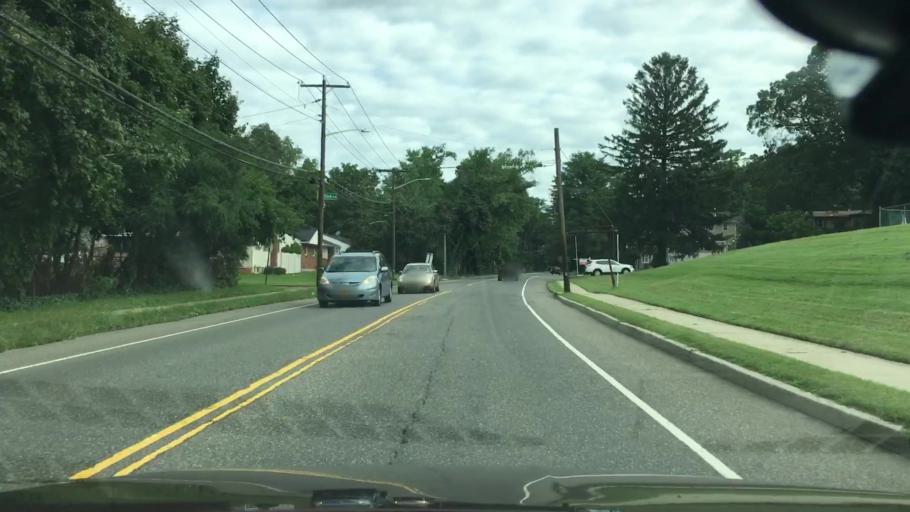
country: US
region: New York
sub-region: Nassau County
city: Old Bethpage
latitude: 40.7701
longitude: -73.4510
